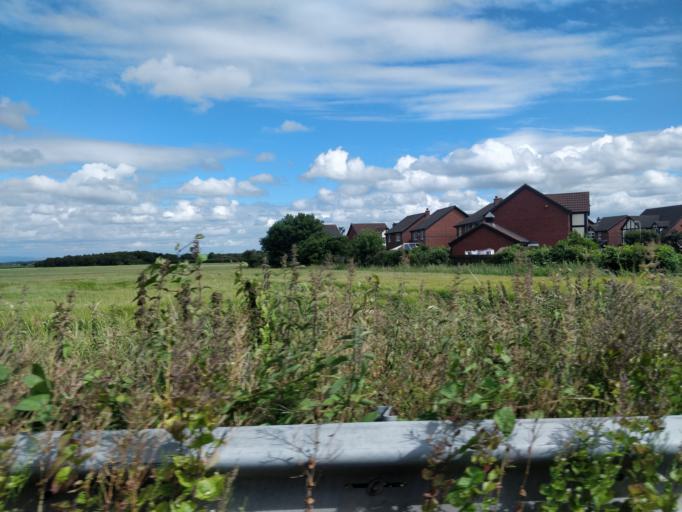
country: GB
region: England
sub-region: Lancashire
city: Banks
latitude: 53.6651
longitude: -2.9530
